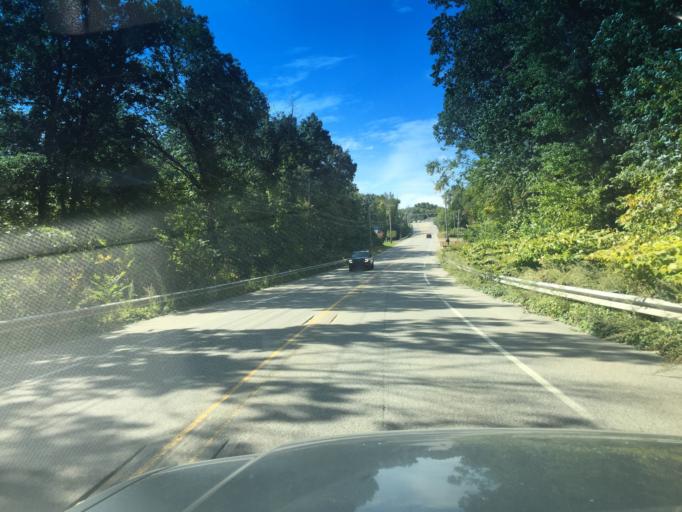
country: US
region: Massachusetts
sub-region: Worcester County
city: Northborough
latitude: 42.2892
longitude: -71.6649
